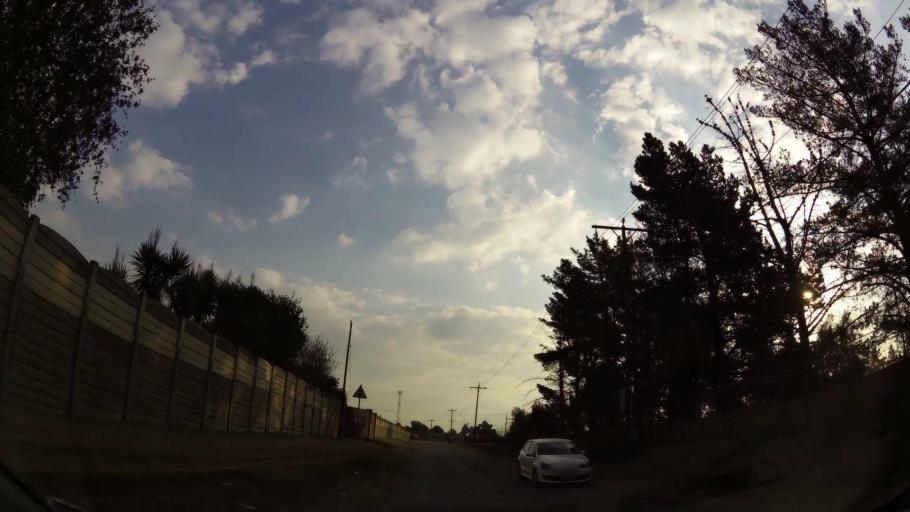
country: ZA
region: Gauteng
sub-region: Ekurhuleni Metropolitan Municipality
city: Benoni
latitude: -26.1207
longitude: 28.2954
